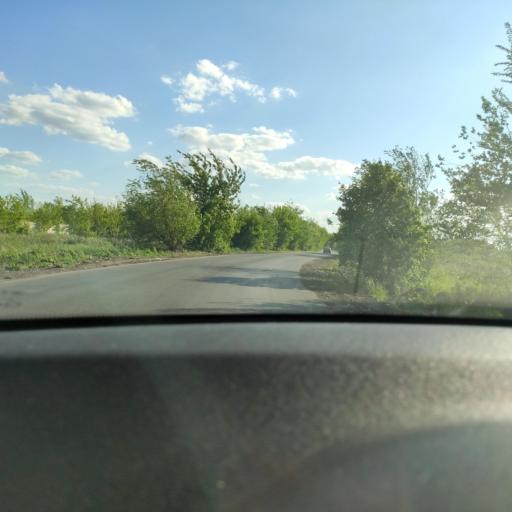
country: RU
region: Samara
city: Smyshlyayevka
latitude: 53.2463
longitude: 50.3650
